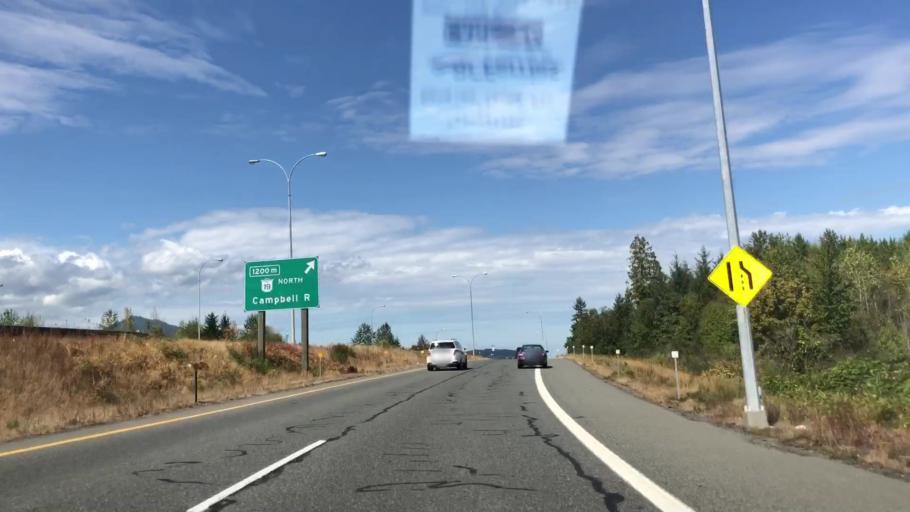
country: CA
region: British Columbia
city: Nanaimo
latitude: 49.1112
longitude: -123.9024
